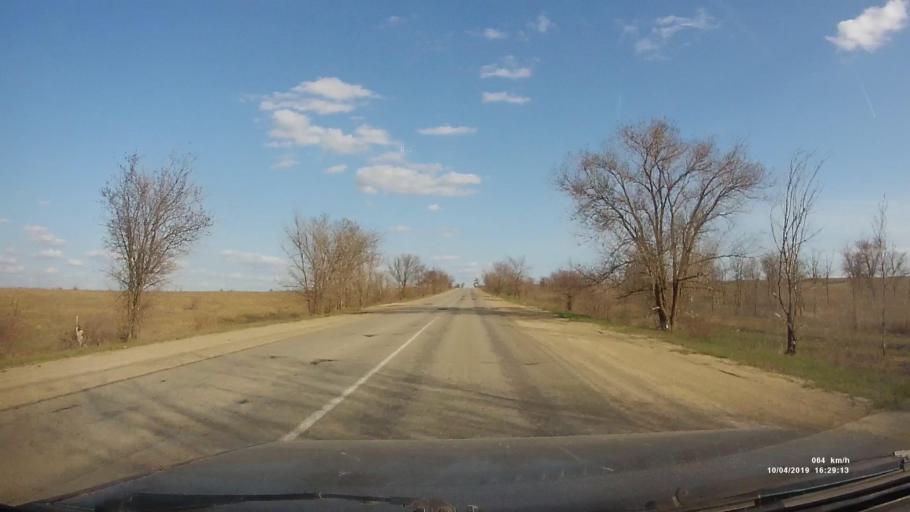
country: RU
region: Rostov
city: Staraya Stanitsa
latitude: 48.2697
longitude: 40.3526
